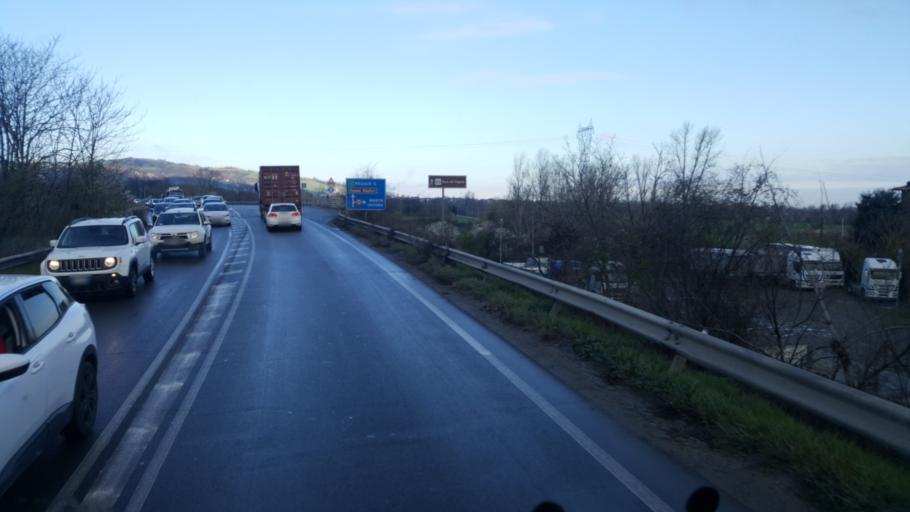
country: IT
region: Emilia-Romagna
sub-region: Provincia di Modena
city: Sassuolo
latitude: 44.5592
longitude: 10.7841
